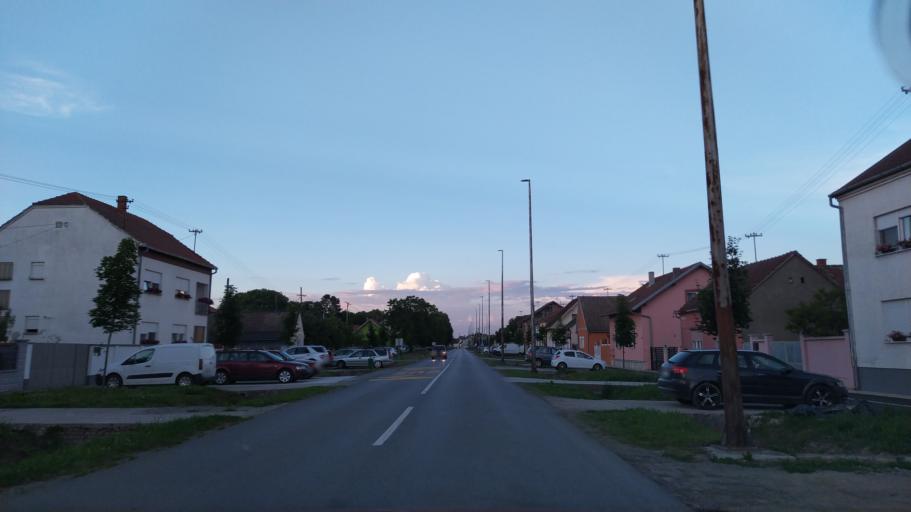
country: HR
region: Osjecko-Baranjska
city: Cepin
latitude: 45.5167
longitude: 18.5479
